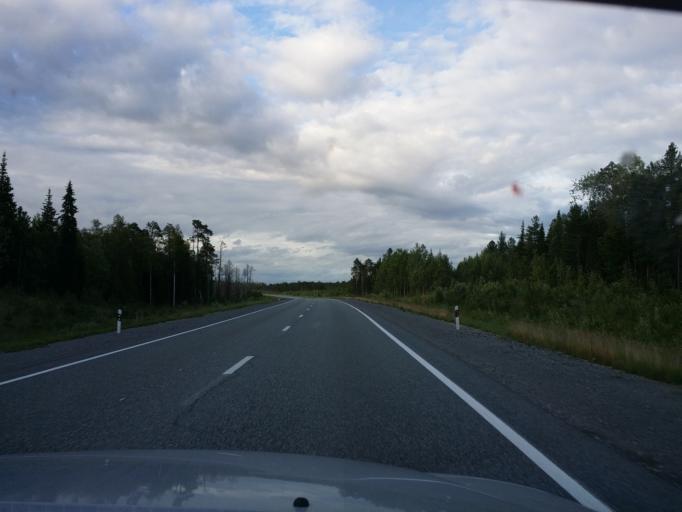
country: RU
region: Khanty-Mansiyskiy Avtonomnyy Okrug
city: Pyt-Yakh
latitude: 60.7037
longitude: 72.5370
